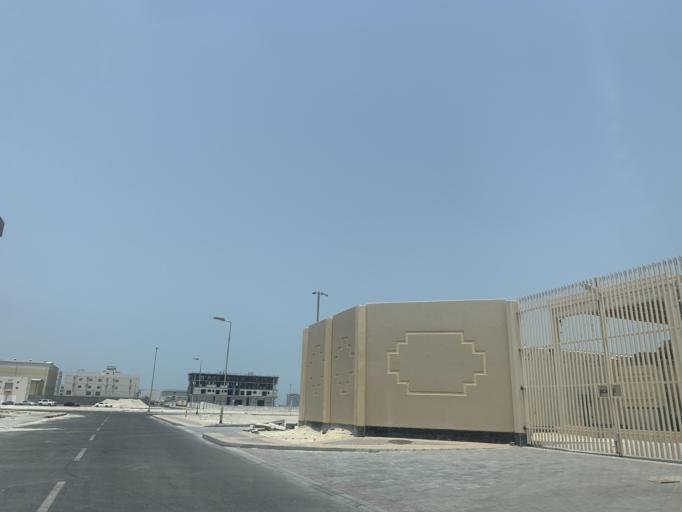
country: BH
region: Muharraq
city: Al Hadd
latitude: 26.2548
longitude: 50.6707
